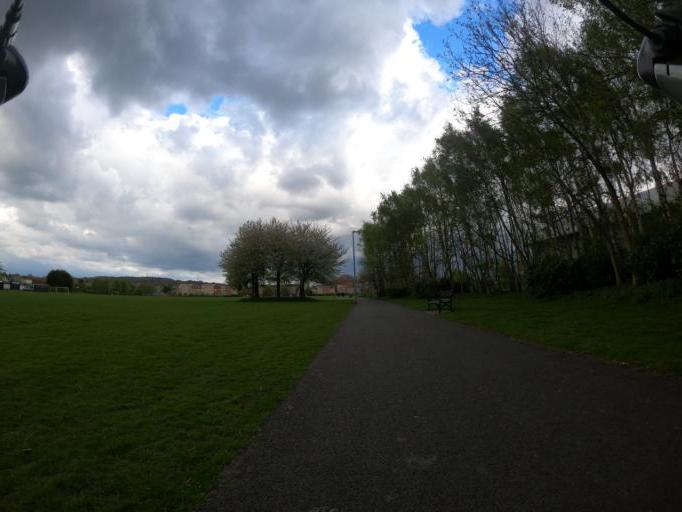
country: GB
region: Scotland
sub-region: Edinburgh
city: Currie
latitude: 55.9396
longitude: -3.3032
